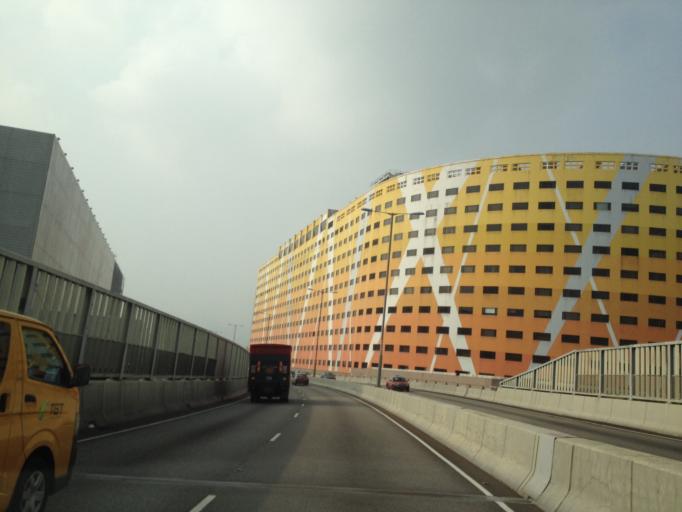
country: HK
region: Kowloon City
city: Kowloon
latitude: 22.3256
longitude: 114.2044
